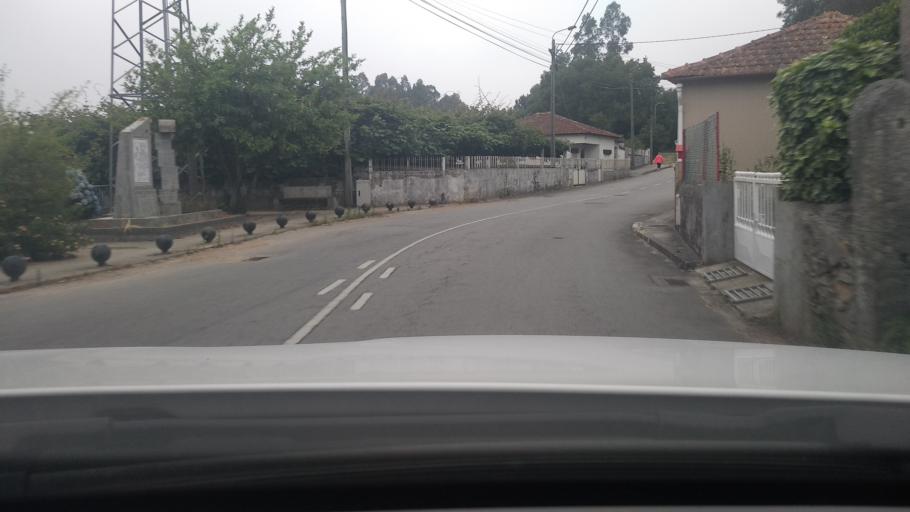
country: PT
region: Aveiro
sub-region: Espinho
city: Silvalde
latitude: 40.9975
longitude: -8.6280
